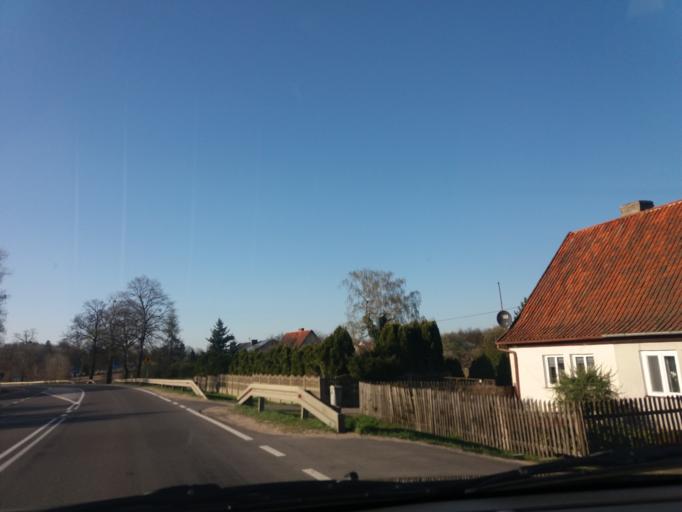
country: PL
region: Warmian-Masurian Voivodeship
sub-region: Powiat nidzicki
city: Nidzica
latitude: 53.3452
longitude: 20.4333
